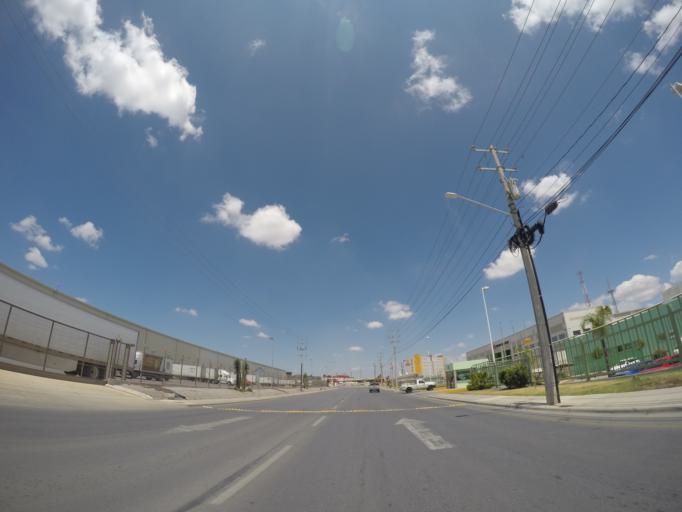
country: MX
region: San Luis Potosi
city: La Pila
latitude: 22.0386
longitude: -100.8911
